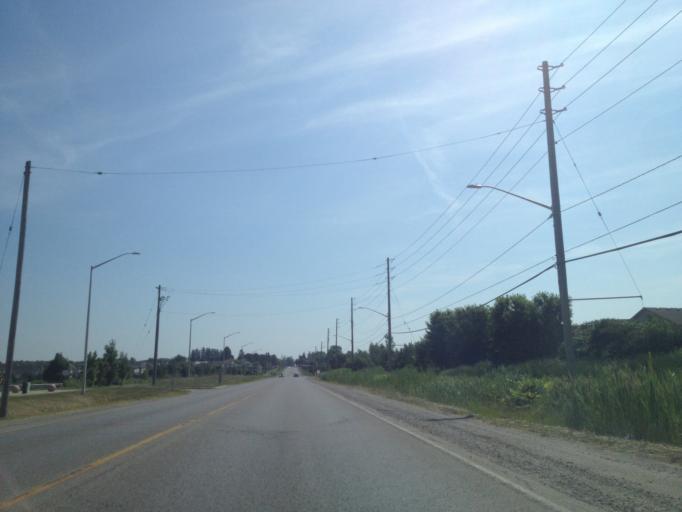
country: CA
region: Ontario
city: London
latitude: 43.0476
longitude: -81.2577
